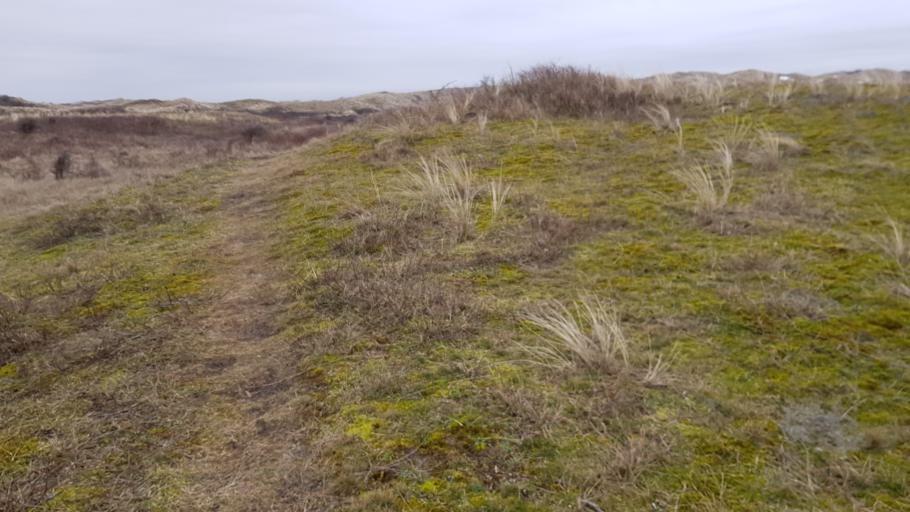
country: NL
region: North Holland
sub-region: Gemeente Bergen
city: Egmond aan Zee
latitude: 52.5904
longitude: 4.6169
